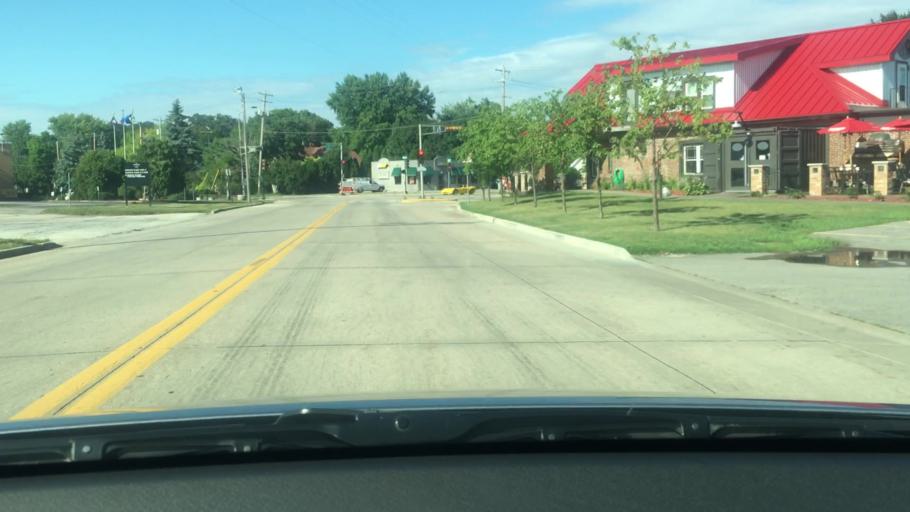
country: US
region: Wisconsin
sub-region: Winnebago County
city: Oshkosh
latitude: 43.9915
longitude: -88.5432
